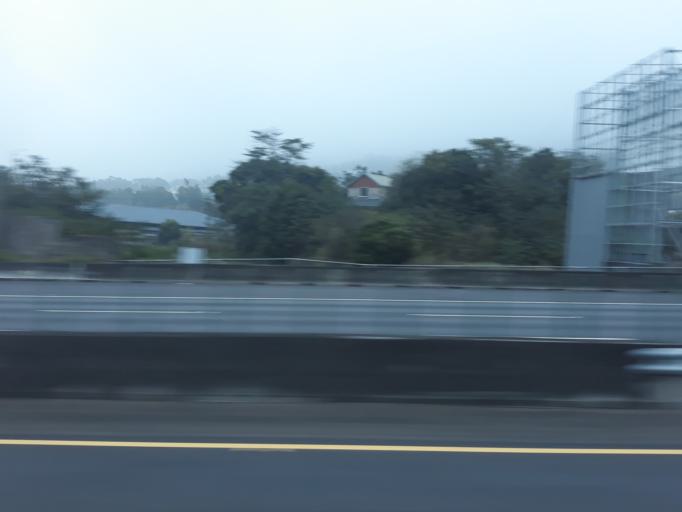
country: TW
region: Taiwan
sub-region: Miaoli
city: Miaoli
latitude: 24.4699
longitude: 120.7877
